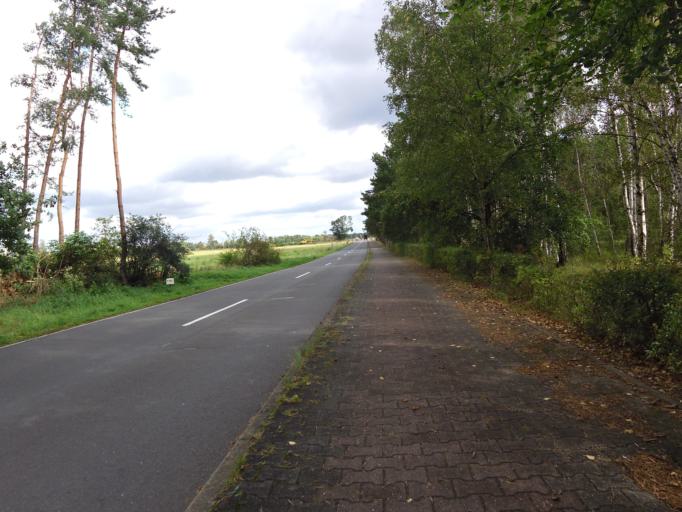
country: DE
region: Saxony-Anhalt
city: Gommern
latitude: 52.0621
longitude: 11.8568
